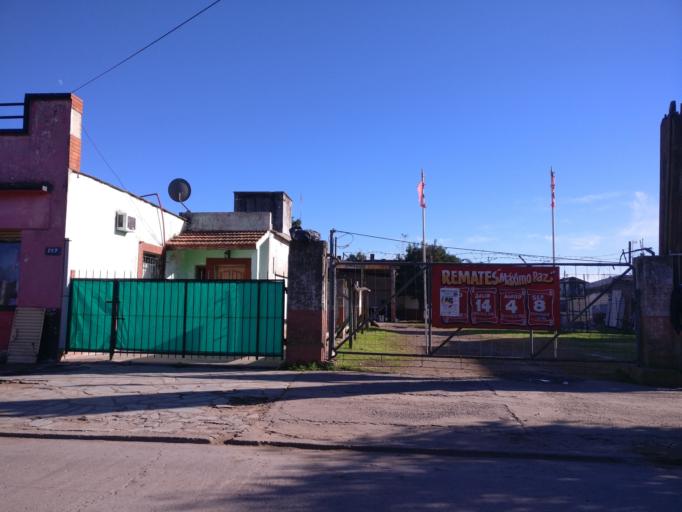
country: AR
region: Buenos Aires
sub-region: Partido de Ezeiza
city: Ezeiza
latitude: -34.9409
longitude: -58.6157
